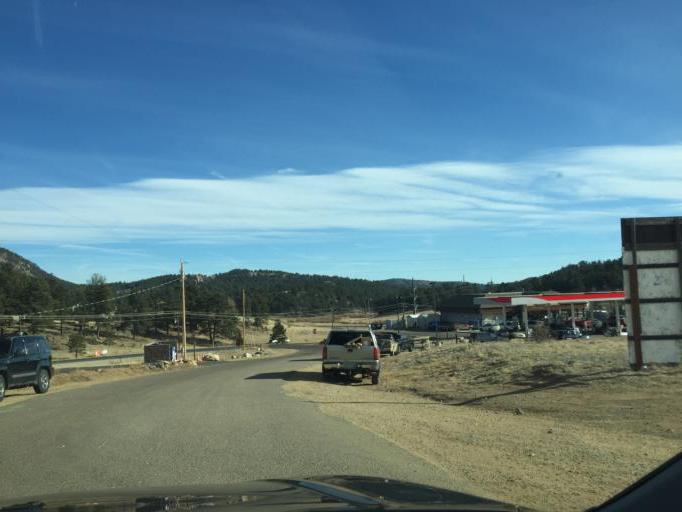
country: US
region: Colorado
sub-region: Jefferson County
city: Evergreen
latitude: 39.4401
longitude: -105.4552
